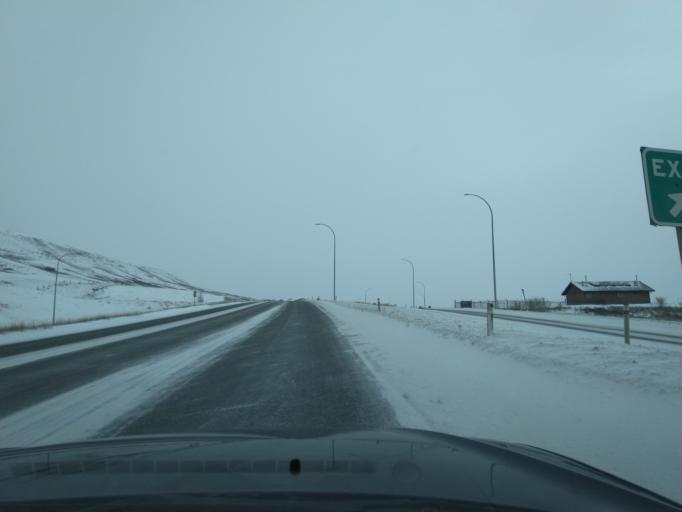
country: CA
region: Alberta
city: Cochrane
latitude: 51.1911
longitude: -114.4543
